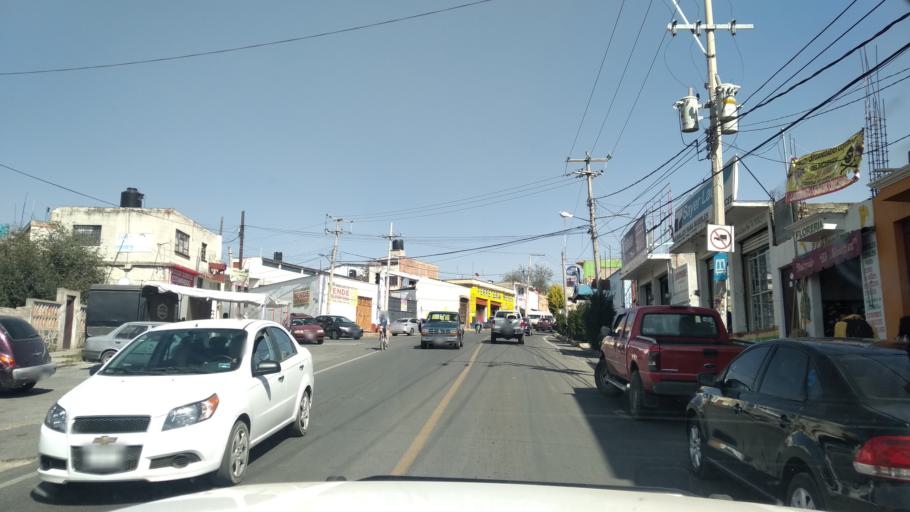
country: MX
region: Hidalgo
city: Calpulalpan
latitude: 19.5889
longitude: -98.5735
